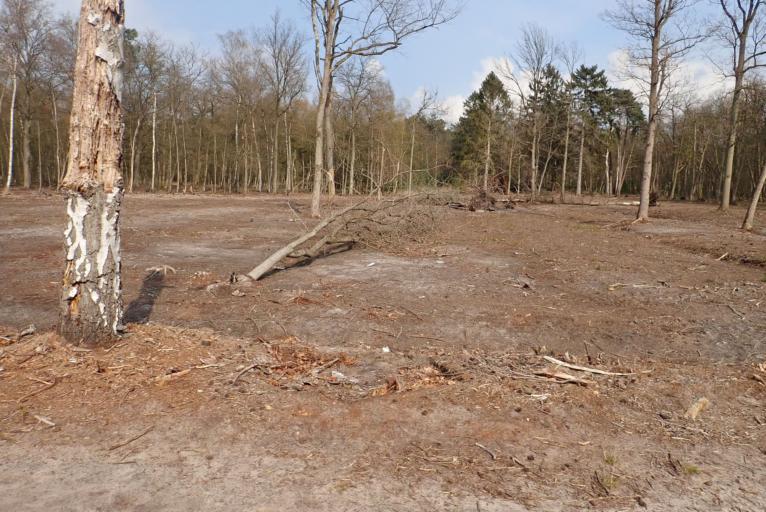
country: BE
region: Flanders
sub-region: Provincie Antwerpen
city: Kalmthout
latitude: 51.4058
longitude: 4.4564
